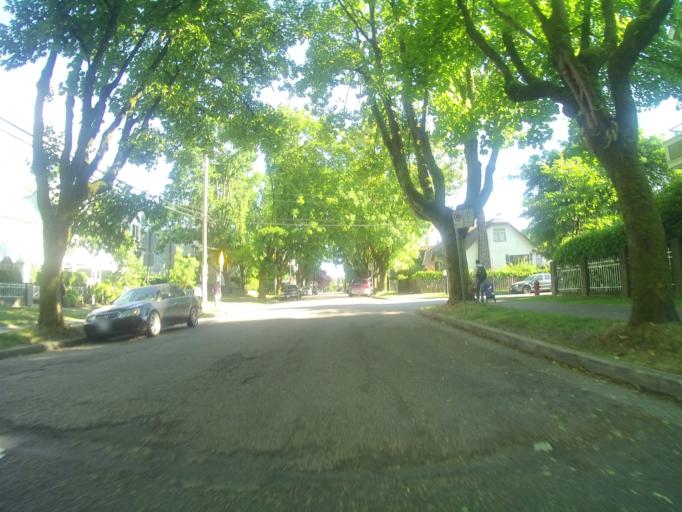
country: CA
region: British Columbia
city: Vancouver
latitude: 49.2581
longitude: -123.1201
